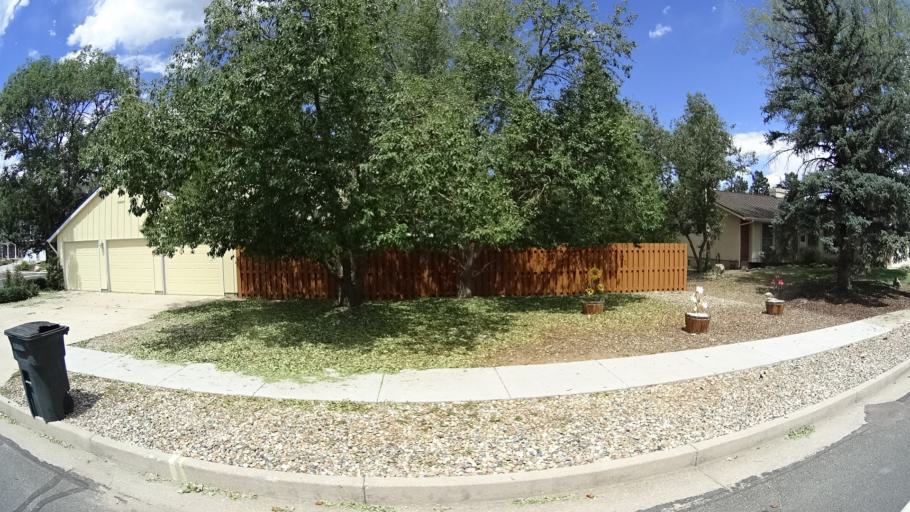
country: US
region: Colorado
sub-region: El Paso County
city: Colorado Springs
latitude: 38.7912
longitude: -104.8339
